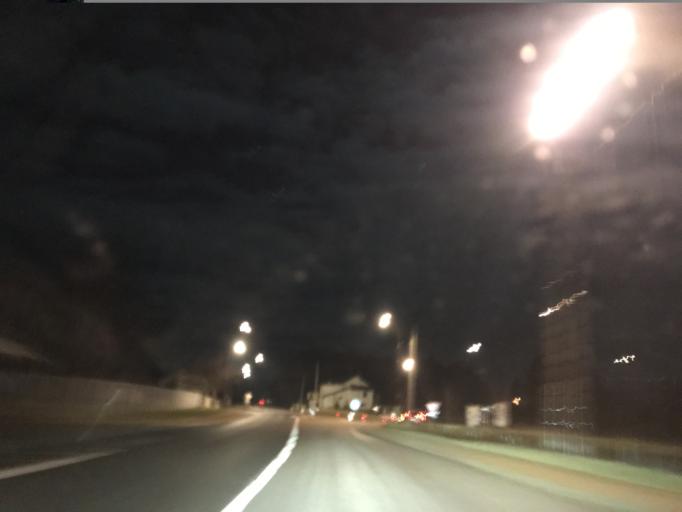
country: FR
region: Auvergne
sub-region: Departement de l'Allier
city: Hauterive
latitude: 46.0953
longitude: 3.4349
